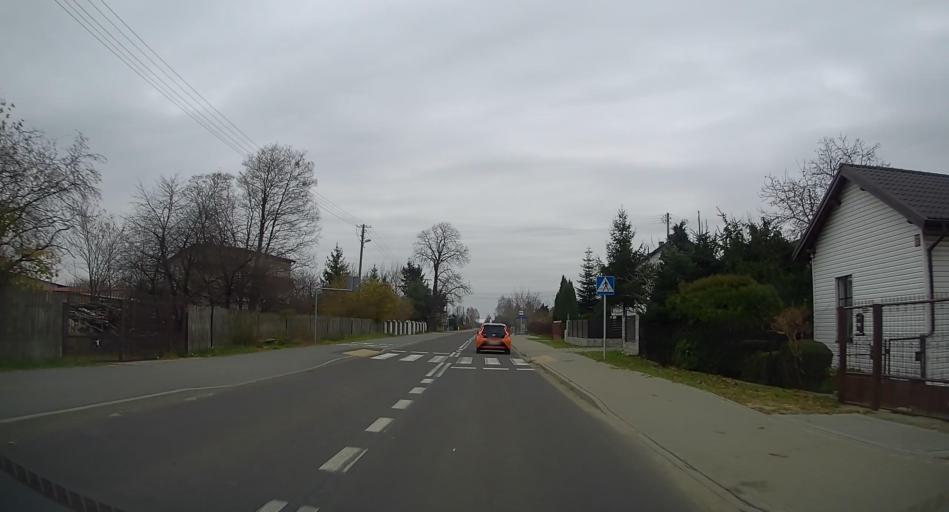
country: PL
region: Masovian Voivodeship
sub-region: Powiat zyrardowski
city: Radziejowice
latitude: 52.0059
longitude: 20.5957
